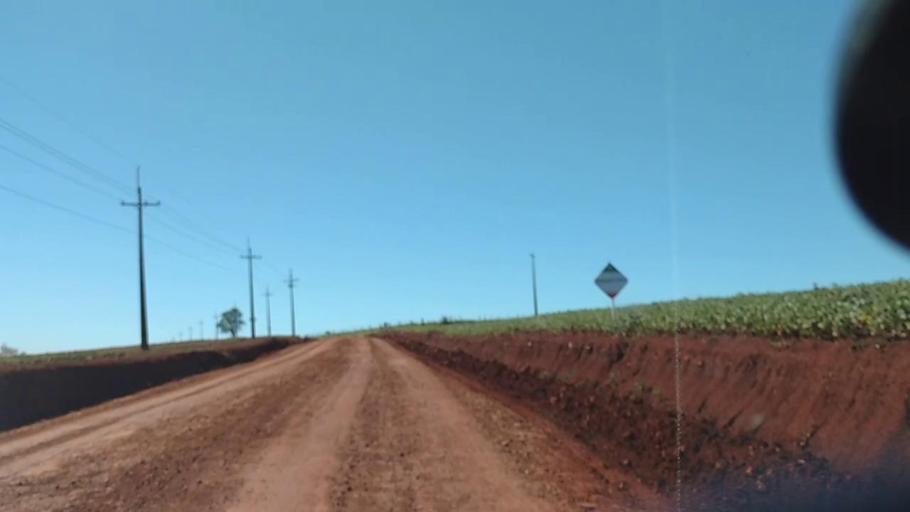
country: PY
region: Alto Parana
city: Naranjal
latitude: -25.9756
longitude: -55.2217
